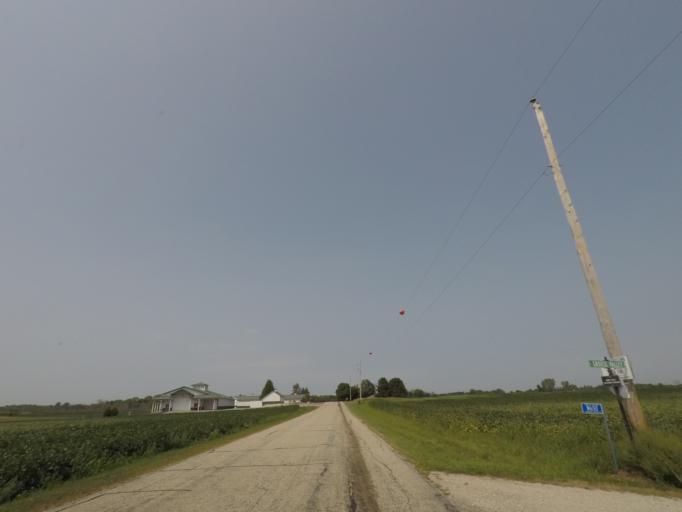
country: US
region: Wisconsin
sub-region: Waukesha County
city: Oconomowoc
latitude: 43.0657
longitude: -88.5675
